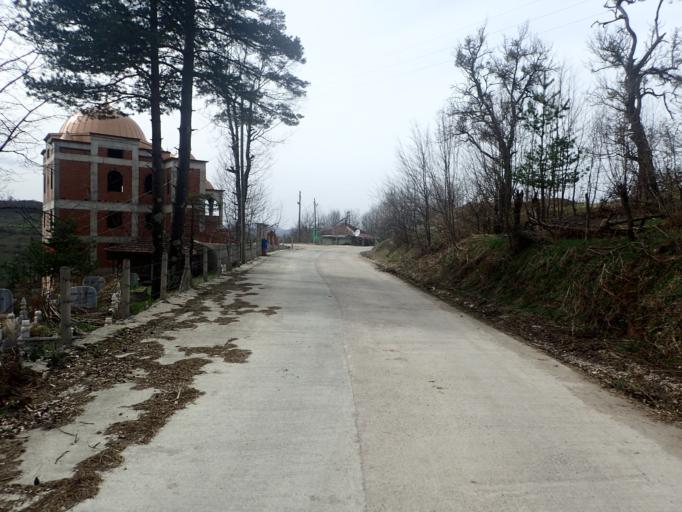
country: TR
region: Ordu
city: Kumru
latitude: 40.8187
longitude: 37.1548
